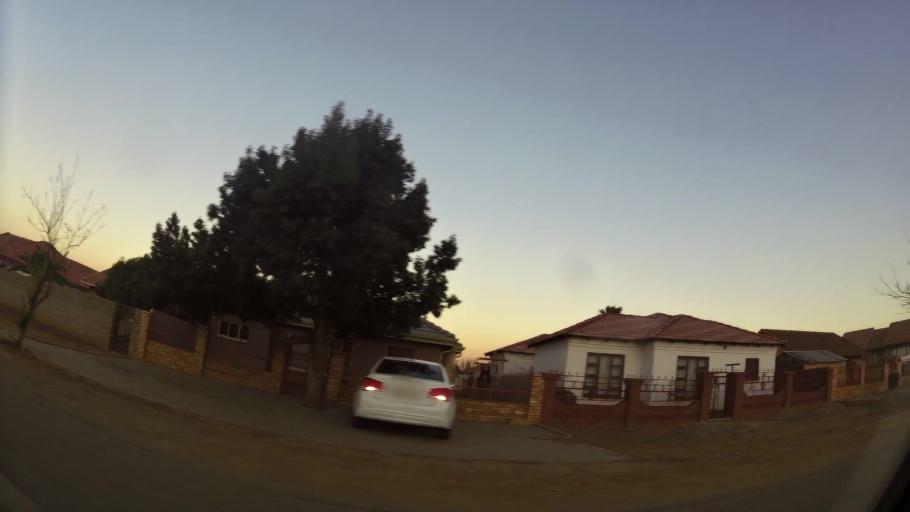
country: ZA
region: North-West
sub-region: Bojanala Platinum District Municipality
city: Rustenburg
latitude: -25.6483
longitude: 27.2072
